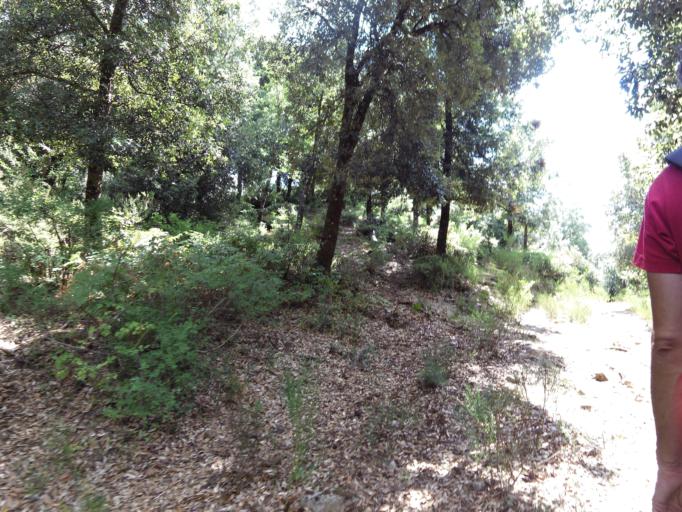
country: IT
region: Calabria
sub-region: Provincia di Vibo-Valentia
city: Nardodipace
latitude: 38.5073
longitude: 16.3884
